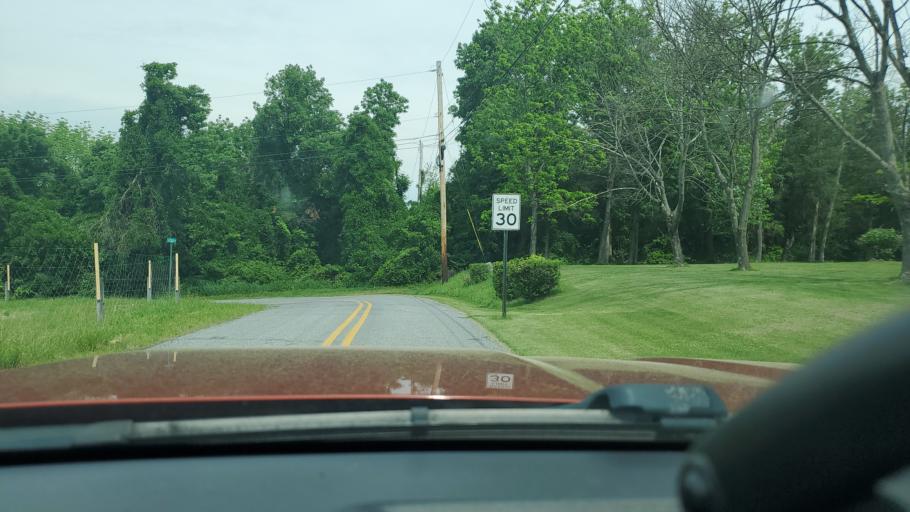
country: US
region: Pennsylvania
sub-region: Montgomery County
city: Woxall
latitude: 40.3165
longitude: -75.5072
